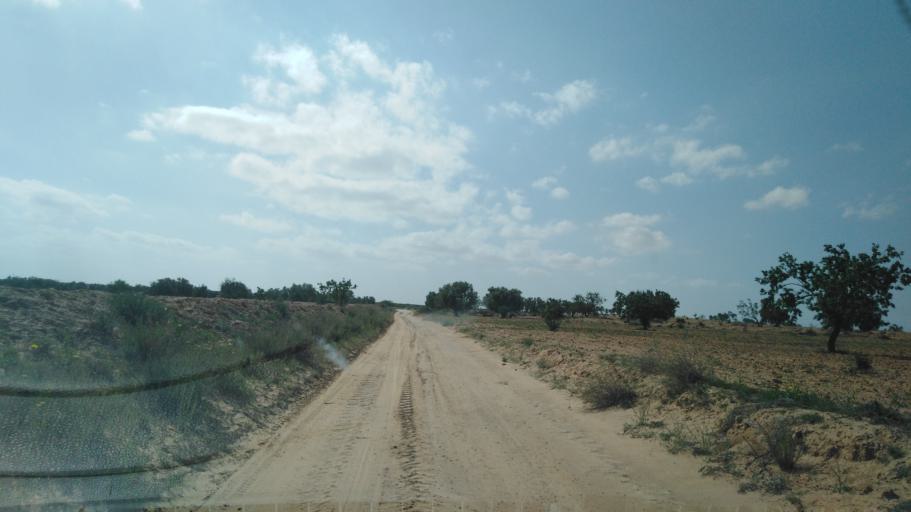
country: TN
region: Safaqis
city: Bi'r `Ali Bin Khalifah
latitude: 34.7996
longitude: 10.3829
